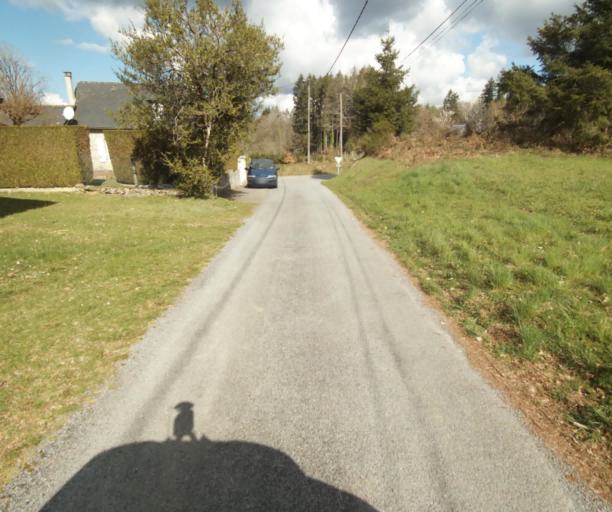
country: FR
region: Limousin
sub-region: Departement de la Correze
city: Argentat
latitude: 45.2245
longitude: 1.9289
